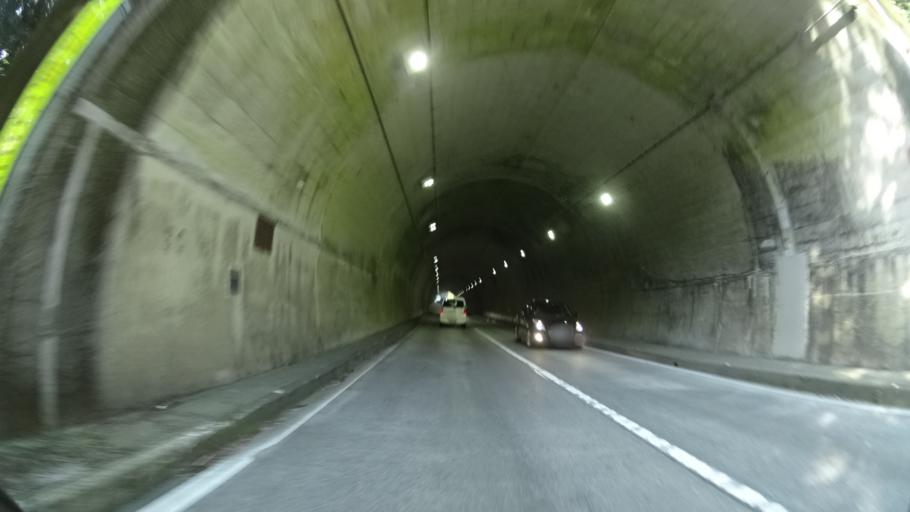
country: JP
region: Ehime
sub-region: Nishiuwa-gun
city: Ikata-cho
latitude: 33.4315
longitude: 132.2124
